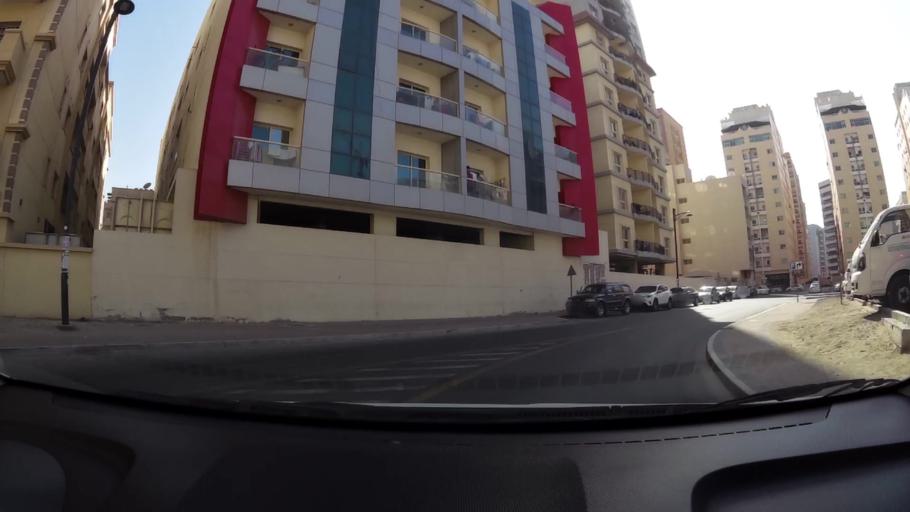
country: AE
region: Ash Shariqah
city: Sharjah
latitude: 25.2934
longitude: 55.3804
